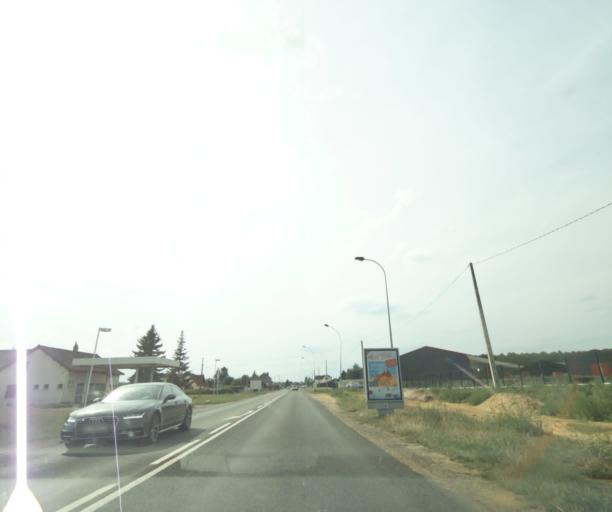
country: FR
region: Pays de la Loire
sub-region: Departement de la Sarthe
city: Ecommoy
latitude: 47.8225
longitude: 0.2928
